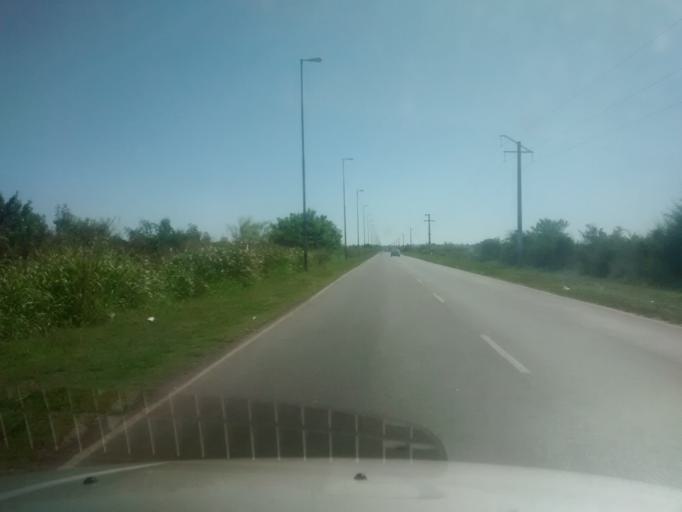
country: AR
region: Buenos Aires
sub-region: Partido de Berisso
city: Berisso
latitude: -34.8938
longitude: -57.8775
